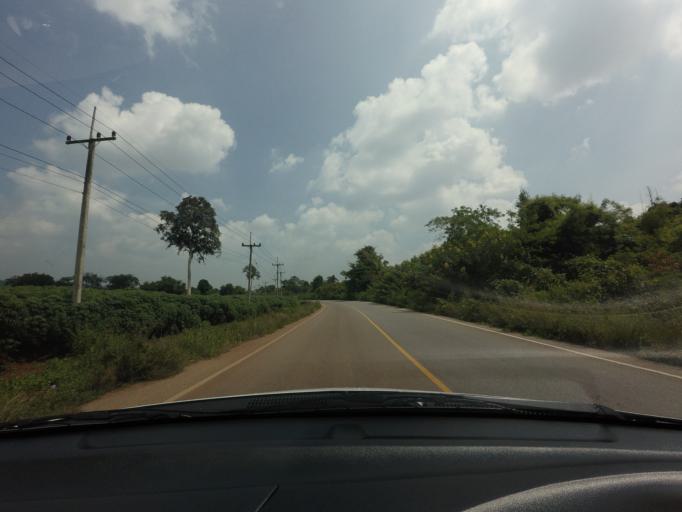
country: TH
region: Nakhon Ratchasima
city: Pak Chong
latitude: 14.5834
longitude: 101.5661
